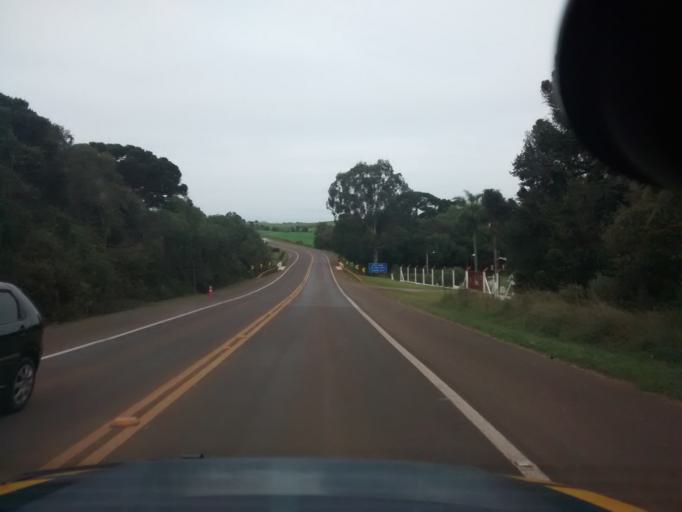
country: BR
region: Rio Grande do Sul
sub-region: Vacaria
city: Vacaria
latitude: -28.4406
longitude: -50.9971
